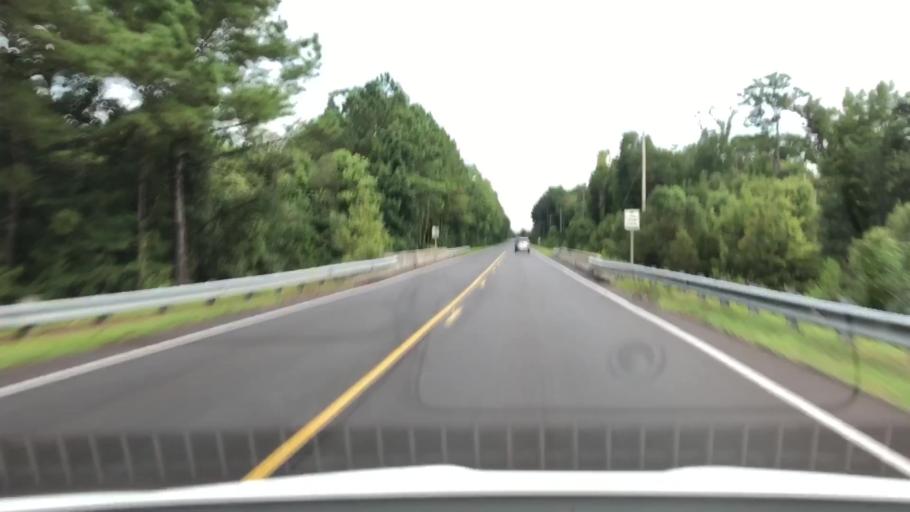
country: US
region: North Carolina
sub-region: Jones County
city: Maysville
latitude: 34.8714
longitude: -77.1961
